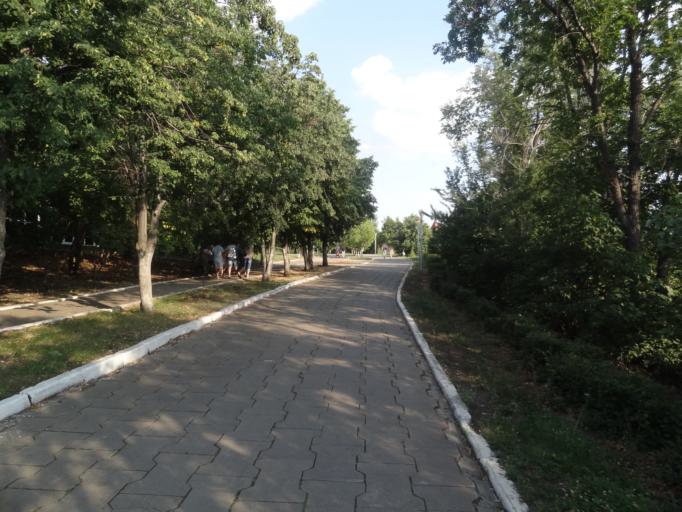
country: RU
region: Saratov
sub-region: Saratovskiy Rayon
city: Saratov
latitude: 51.5429
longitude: 46.0542
